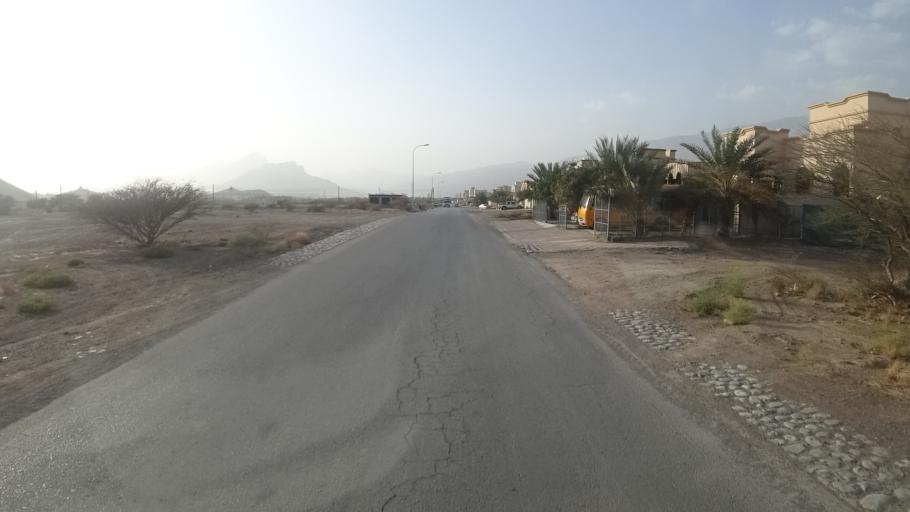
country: OM
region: Muhafazat ad Dakhiliyah
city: Bahla'
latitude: 23.0885
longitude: 57.3166
